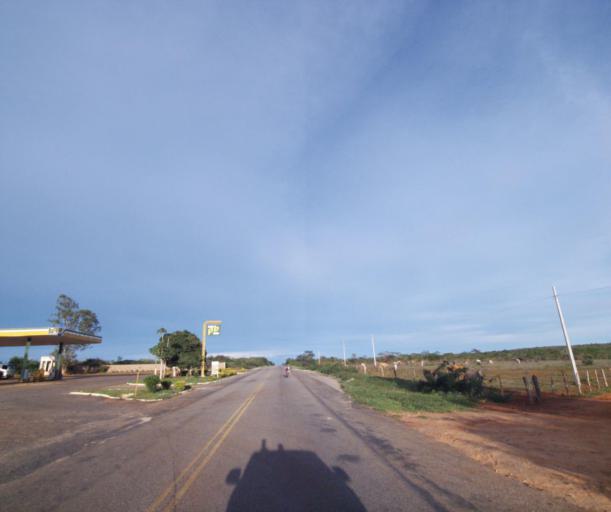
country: BR
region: Bahia
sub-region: Cacule
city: Cacule
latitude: -14.2106
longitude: -42.0944
